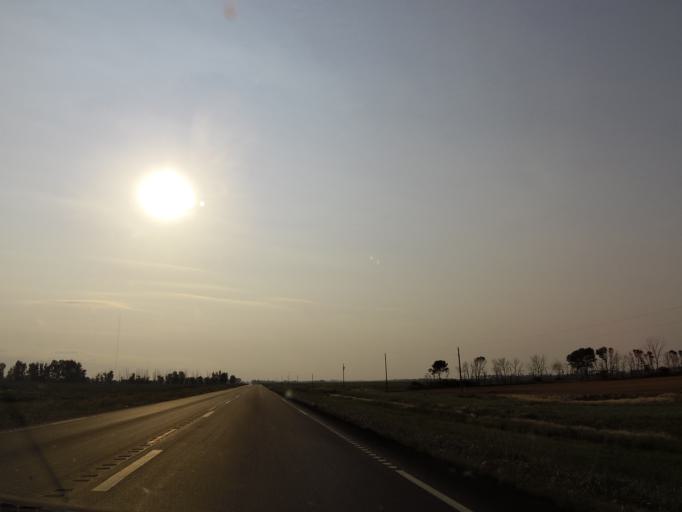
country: US
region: North Dakota
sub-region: Traill County
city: Hillsboro
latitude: 47.3530
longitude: -97.2275
